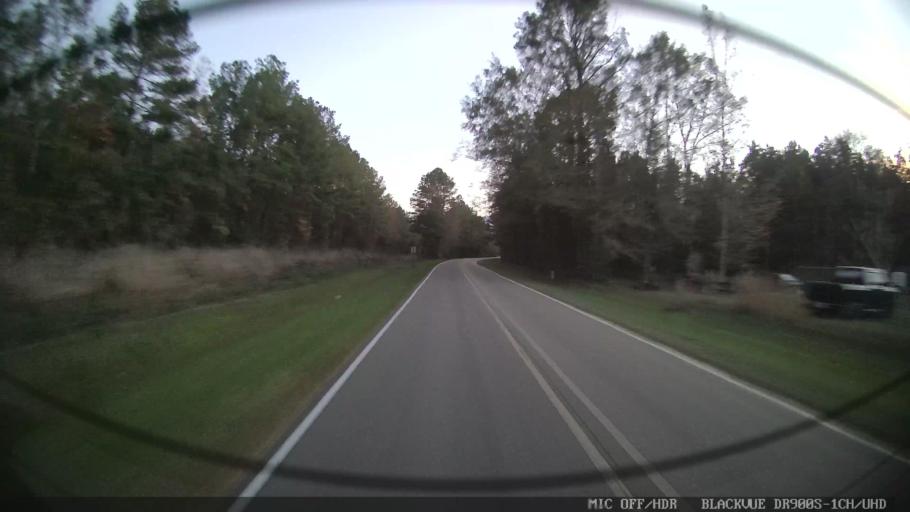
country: US
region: Mississippi
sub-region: Perry County
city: New Augusta
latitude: 31.0887
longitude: -89.1882
